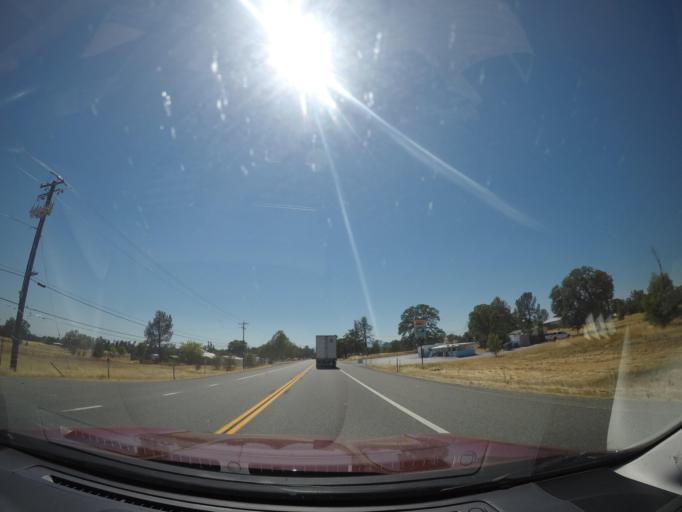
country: US
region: California
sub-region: Shasta County
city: Bella Vista
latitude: 40.6332
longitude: -122.2606
